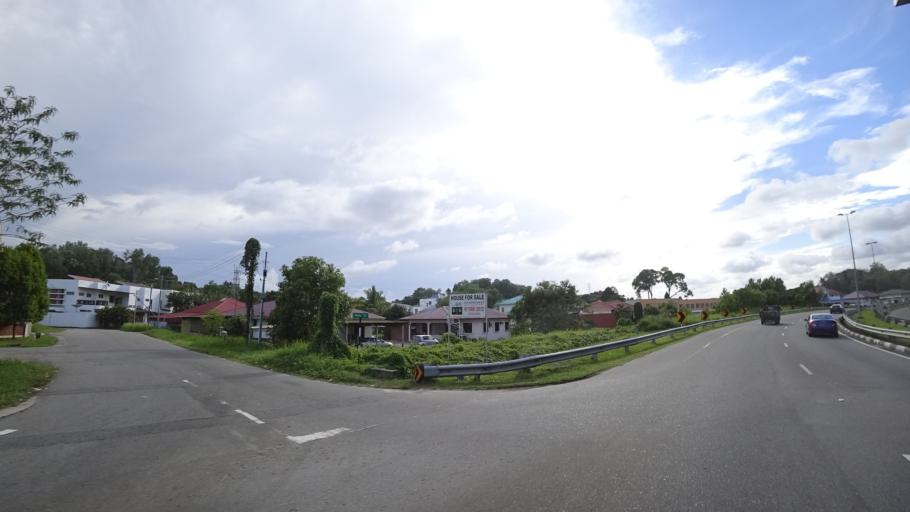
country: BN
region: Brunei and Muara
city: Bandar Seri Begawan
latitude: 4.8791
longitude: 114.8787
